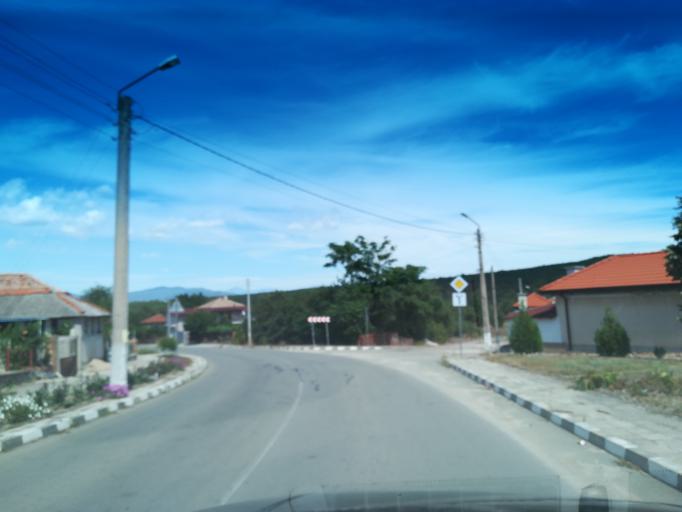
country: BG
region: Plovdiv
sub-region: Obshtina Suedinenie
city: Suedinenie
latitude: 42.4260
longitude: 24.5340
